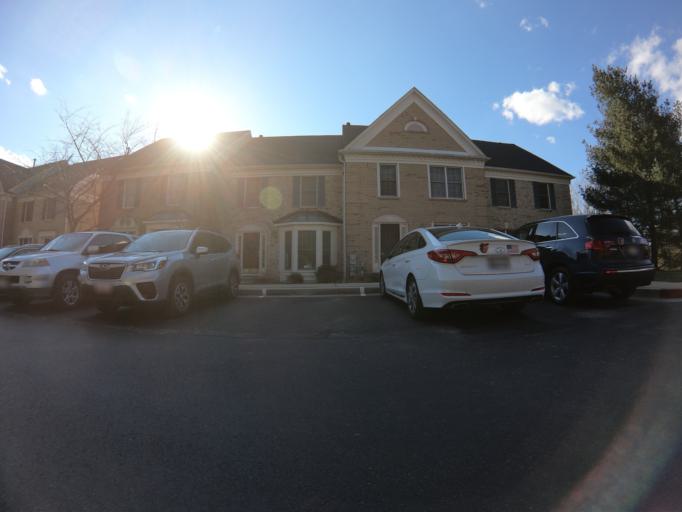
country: US
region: Maryland
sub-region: Howard County
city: Ellicott City
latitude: 39.2563
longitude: -76.8031
